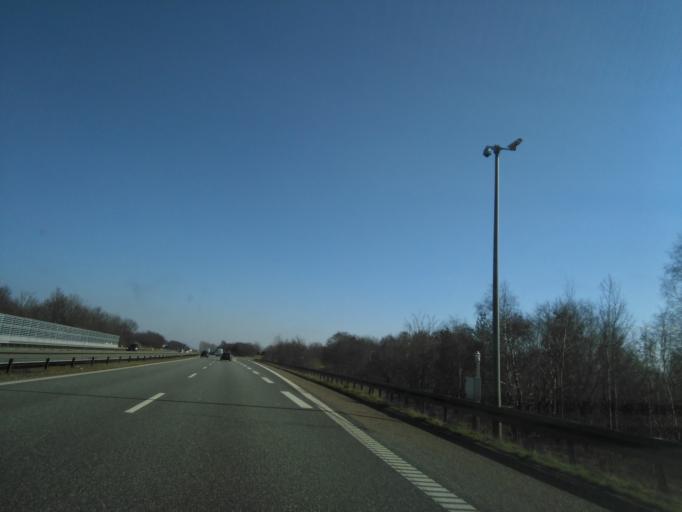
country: DK
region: South Denmark
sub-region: Kerteminde Kommune
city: Langeskov
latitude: 55.3497
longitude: 10.5873
